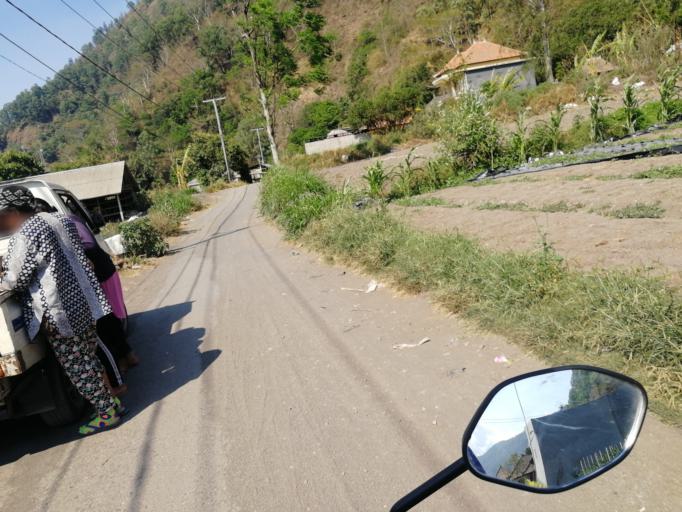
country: ID
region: Bali
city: Banjar Trunyan
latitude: -8.2640
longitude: 115.4211
